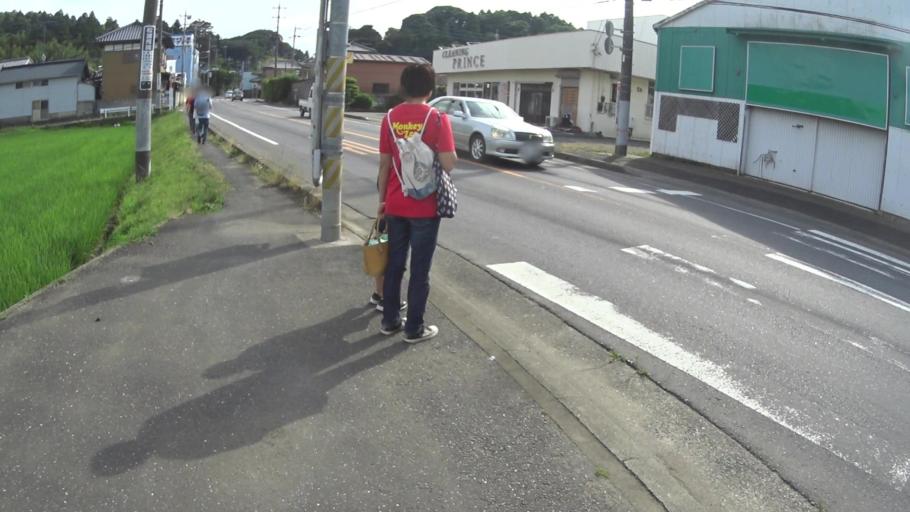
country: JP
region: Chiba
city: Sawara
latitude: 35.8840
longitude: 140.5011
